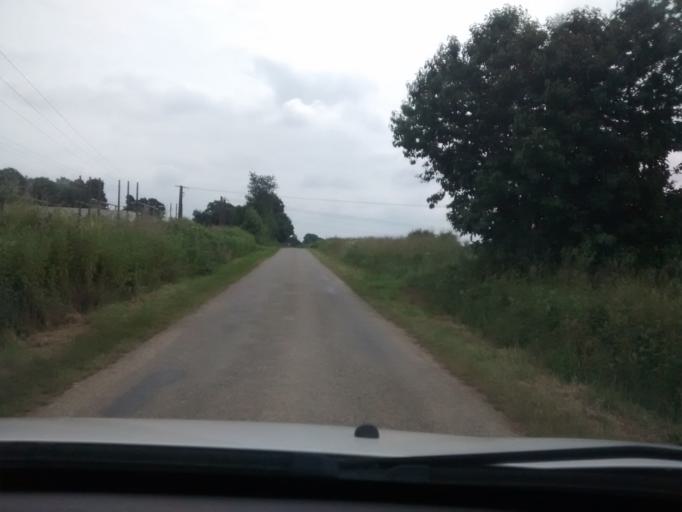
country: FR
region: Brittany
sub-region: Departement d'Ille-et-Vilaine
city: Servon-sur-Vilaine
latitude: 48.1334
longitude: -1.4721
